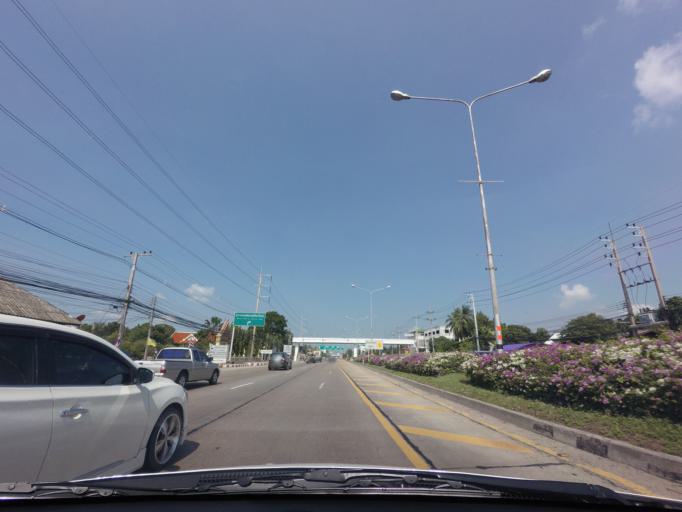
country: TH
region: Nakhon Pathom
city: Nakhon Chai Si
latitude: 13.7871
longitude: 100.1728
